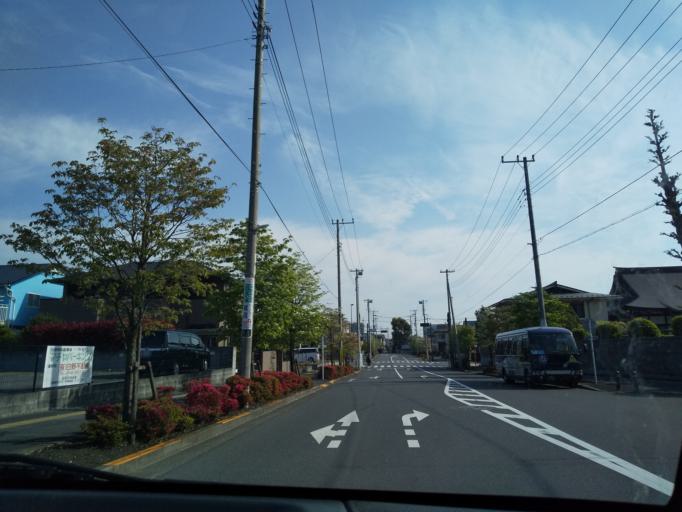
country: JP
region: Tokyo
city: Hino
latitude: 35.6822
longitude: 139.3942
